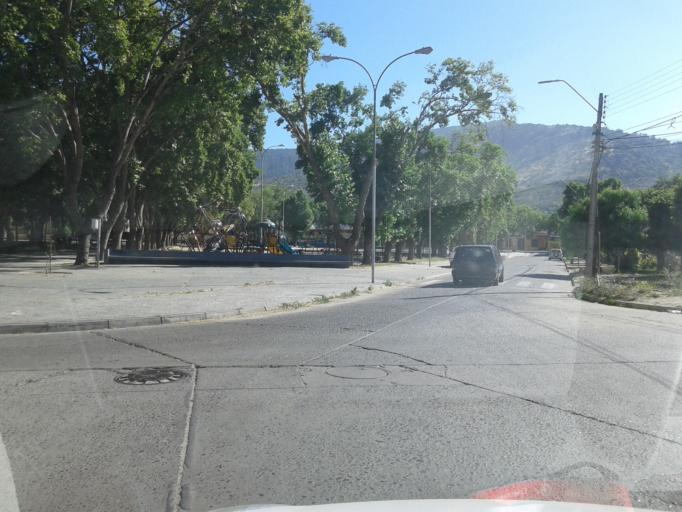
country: CL
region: Valparaiso
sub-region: Provincia de Marga Marga
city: Limache
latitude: -32.9881
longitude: -71.2733
